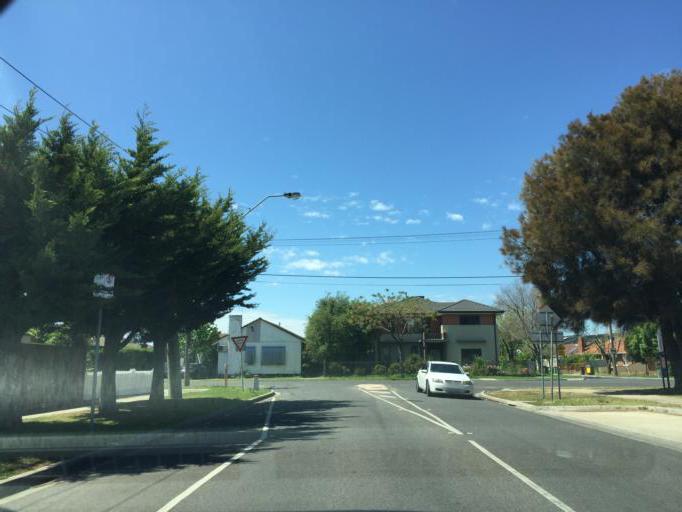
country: AU
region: Victoria
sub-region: Maribyrnong
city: Braybrook
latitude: -37.7828
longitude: 144.8461
